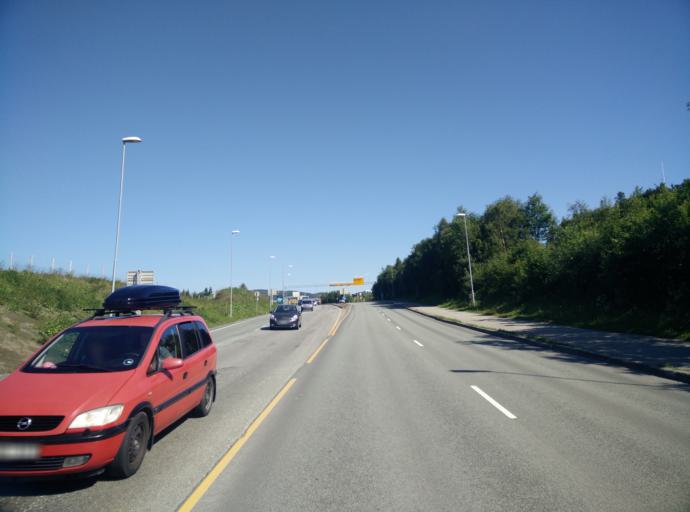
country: NO
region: Sor-Trondelag
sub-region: Trondheim
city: Trondheim
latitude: 63.3704
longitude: 10.3719
